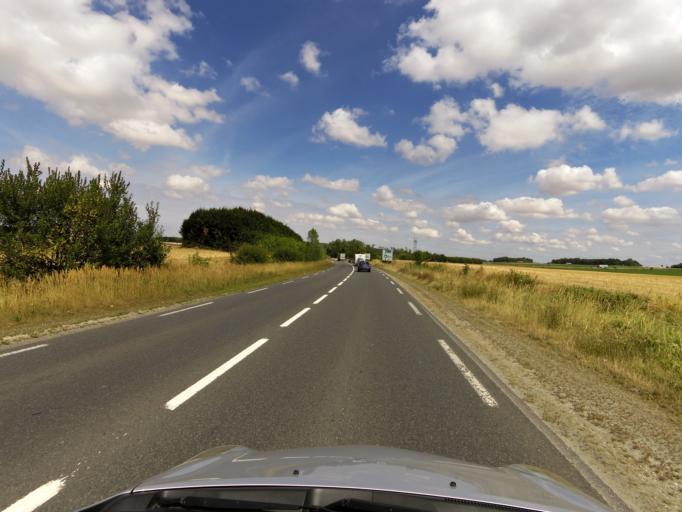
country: FR
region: Ile-de-France
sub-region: Departement de Seine-et-Marne
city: Cregy-les-Meaux
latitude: 48.9849
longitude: 2.8702
